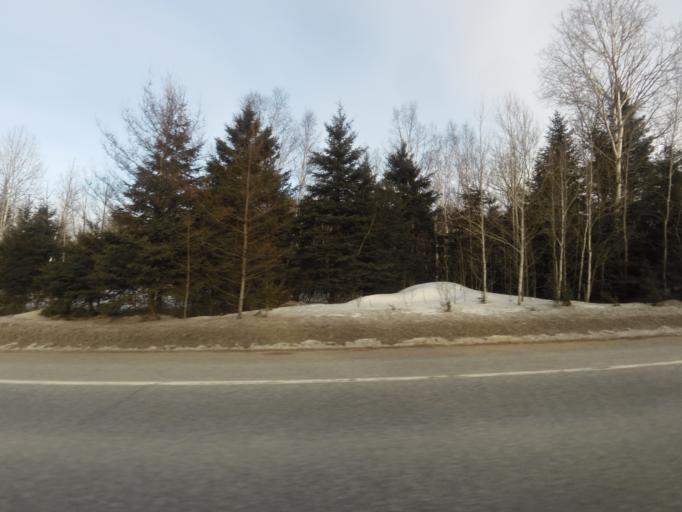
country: CA
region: Quebec
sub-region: Outaouais
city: Wakefield
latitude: 45.8833
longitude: -76.0276
